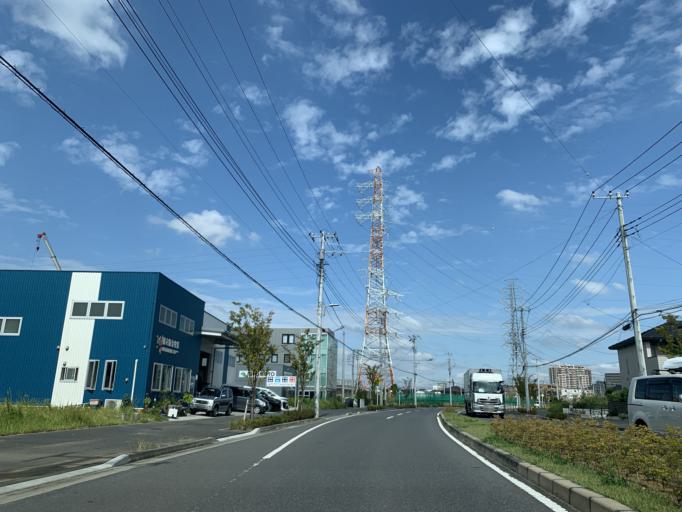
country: JP
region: Chiba
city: Nagareyama
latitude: 35.8601
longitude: 139.9167
